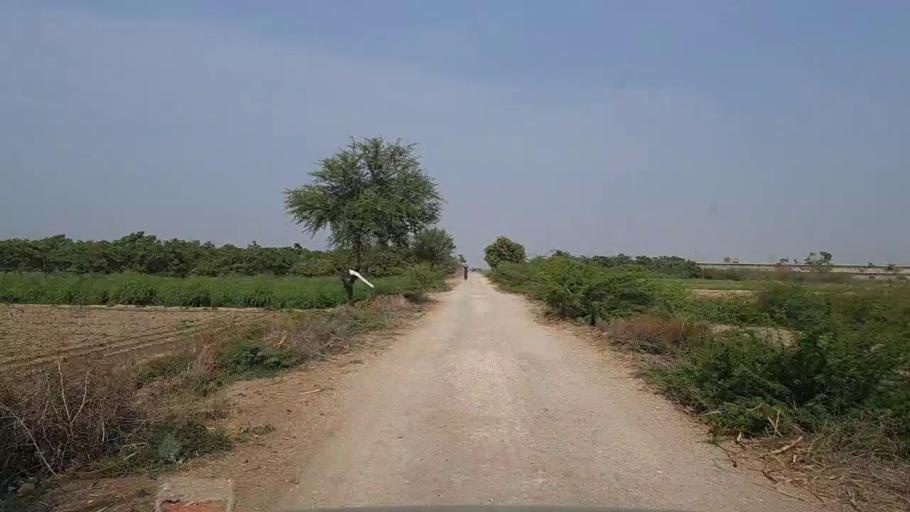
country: PK
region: Sindh
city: Mirwah Gorchani
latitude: 25.3463
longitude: 69.0637
